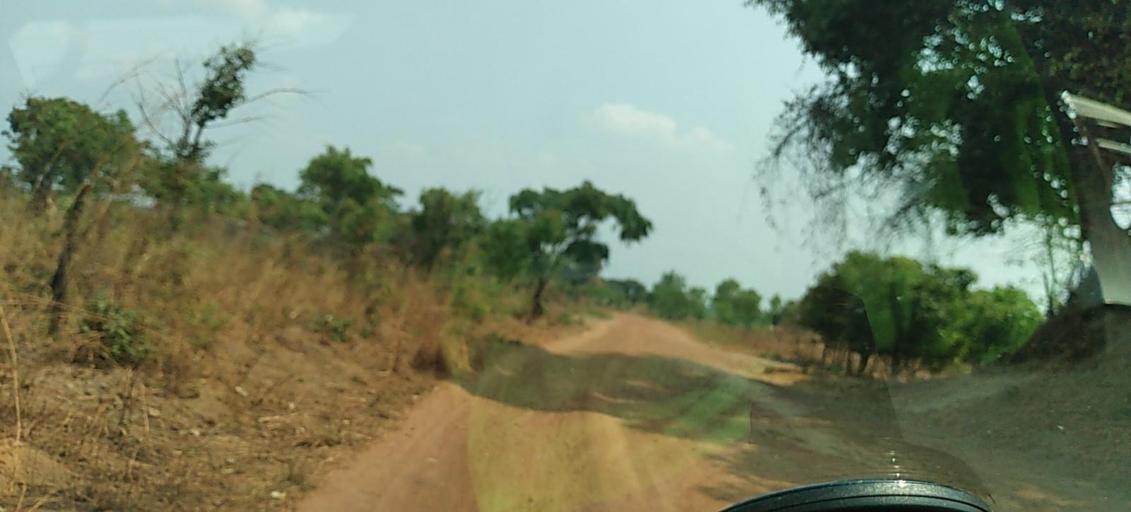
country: ZM
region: North-Western
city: Kansanshi
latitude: -12.0957
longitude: 26.3633
